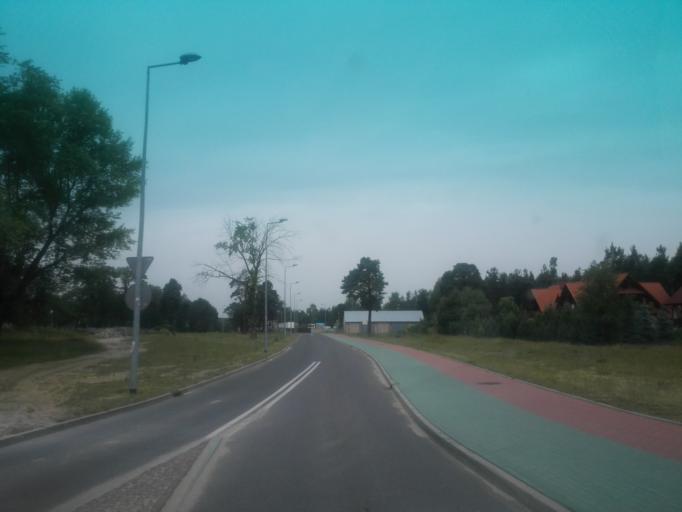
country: PL
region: Silesian Voivodeship
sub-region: Powiat czestochowski
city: Olsztyn
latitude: 50.7538
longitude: 19.2725
